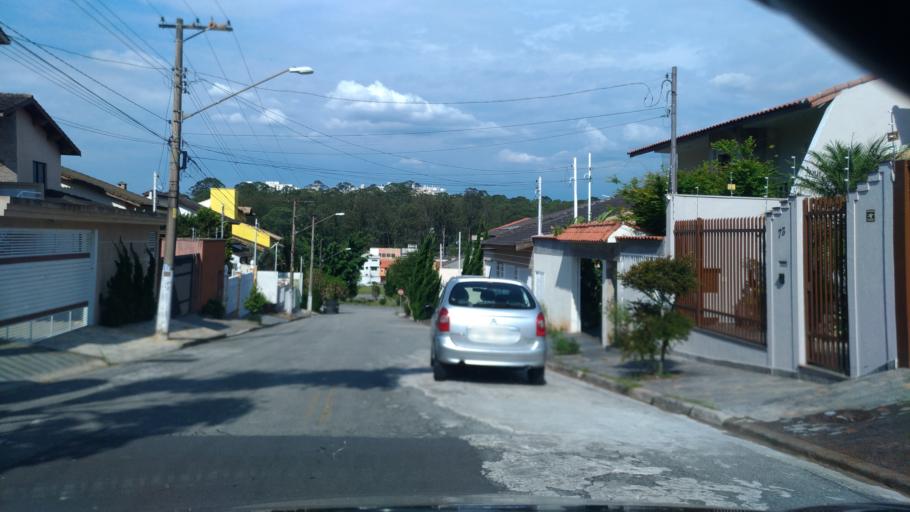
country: BR
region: Sao Paulo
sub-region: Sao Bernardo Do Campo
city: Sao Bernardo do Campo
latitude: -23.7094
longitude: -46.5784
